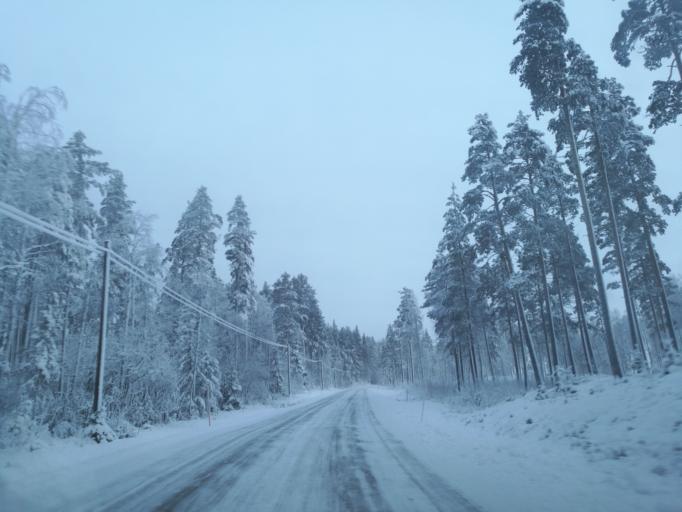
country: NO
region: Hedmark
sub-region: Grue
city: Kirkenaer
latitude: 60.4351
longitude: 12.4558
